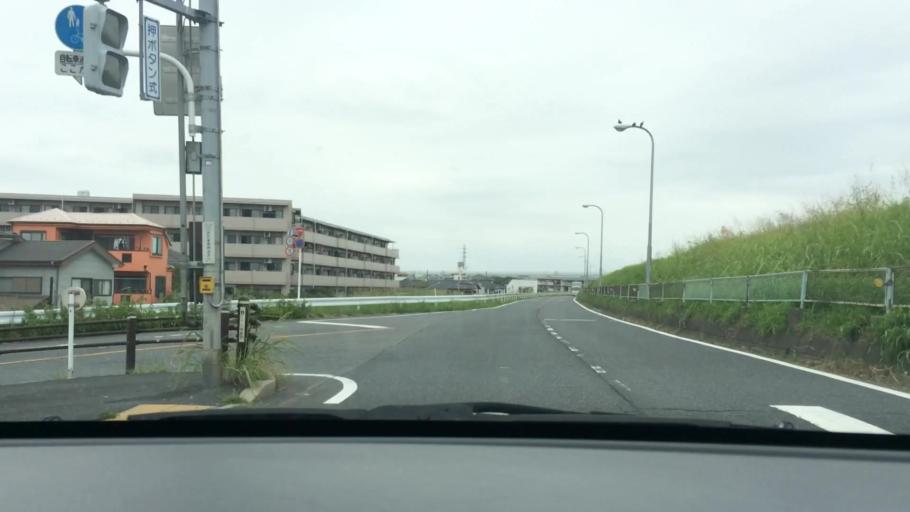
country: JP
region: Chiba
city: Matsudo
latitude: 35.7728
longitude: 139.8799
